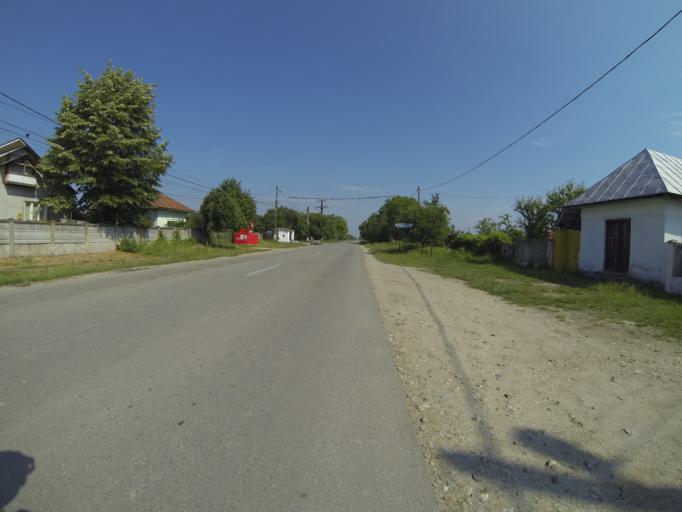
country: RO
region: Gorj
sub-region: Comuna Crusetu
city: Crusetu
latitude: 44.6053
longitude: 23.6896
